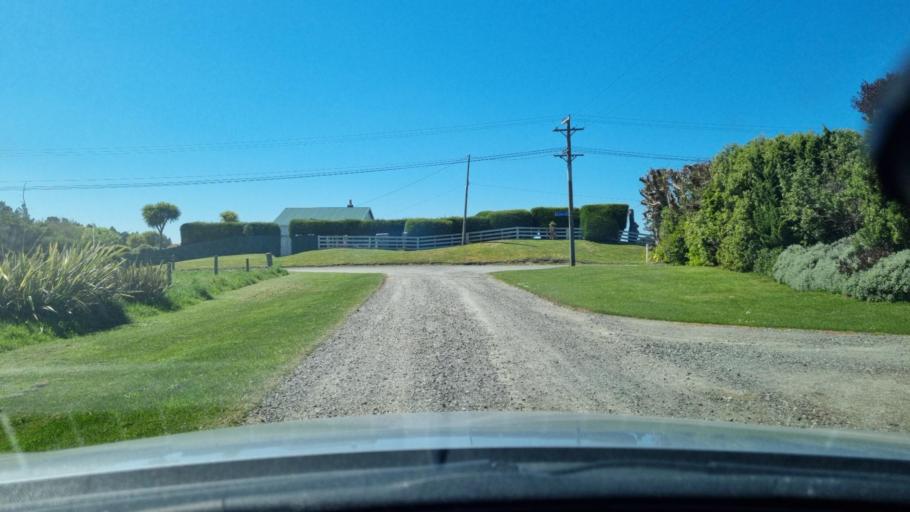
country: NZ
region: Southland
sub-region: Invercargill City
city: Invercargill
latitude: -46.4416
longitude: 168.2923
